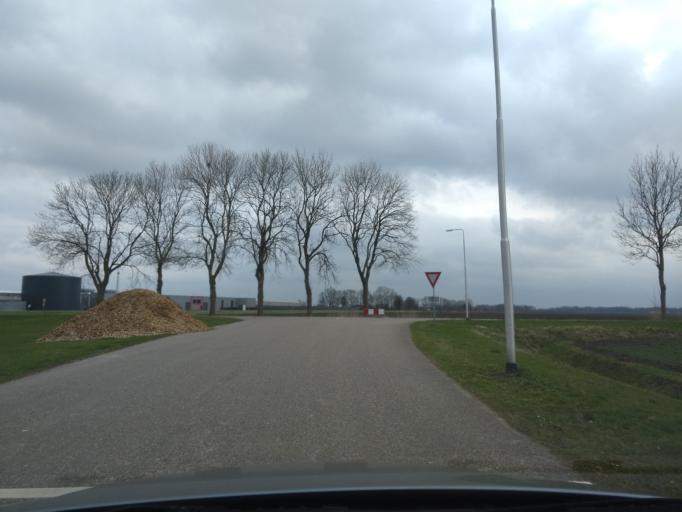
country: NL
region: Overijssel
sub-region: Gemeente Steenwijkerland
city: Blokzijl
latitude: 52.7370
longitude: 5.8574
